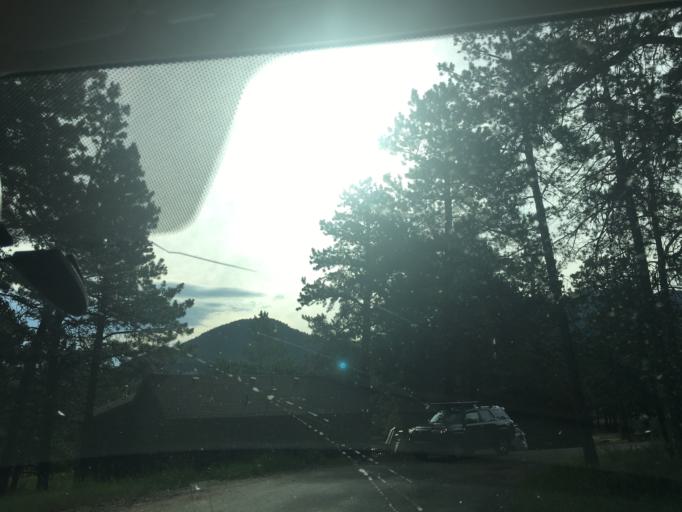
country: US
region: Colorado
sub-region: Larimer County
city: Estes Park
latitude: 40.3427
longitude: -105.5775
